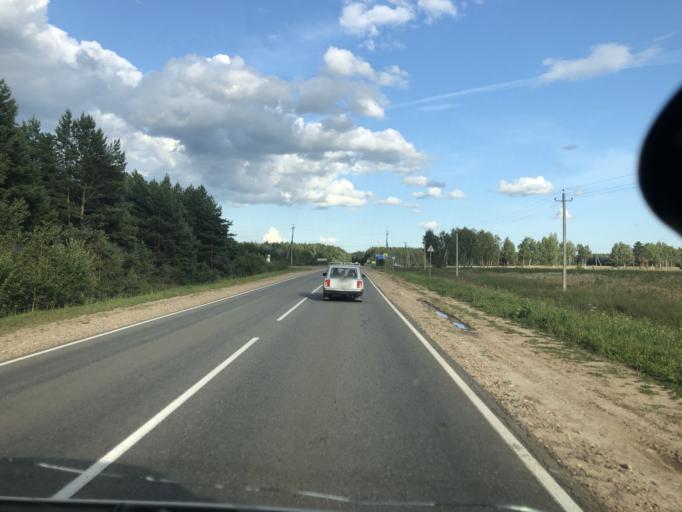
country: RU
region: Kaluga
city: Yukhnov
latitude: 54.7196
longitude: 35.2252
